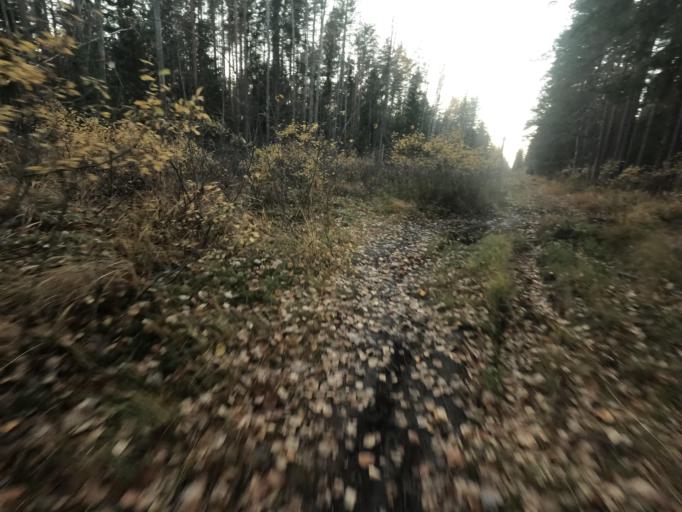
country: RU
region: St.-Petersburg
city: Komarovo
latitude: 60.2027
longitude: 29.8040
